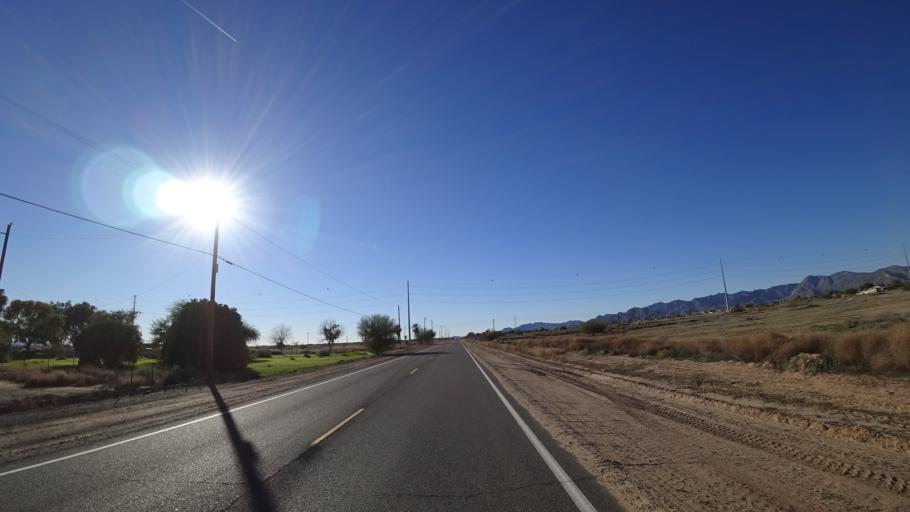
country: US
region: Arizona
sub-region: Maricopa County
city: Citrus Park
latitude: 33.4502
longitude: -112.4588
